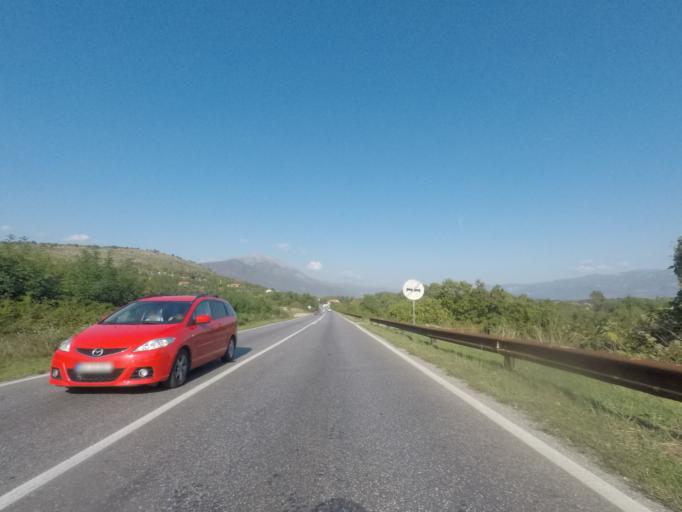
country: ME
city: Spuz
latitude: 42.5021
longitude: 19.1450
